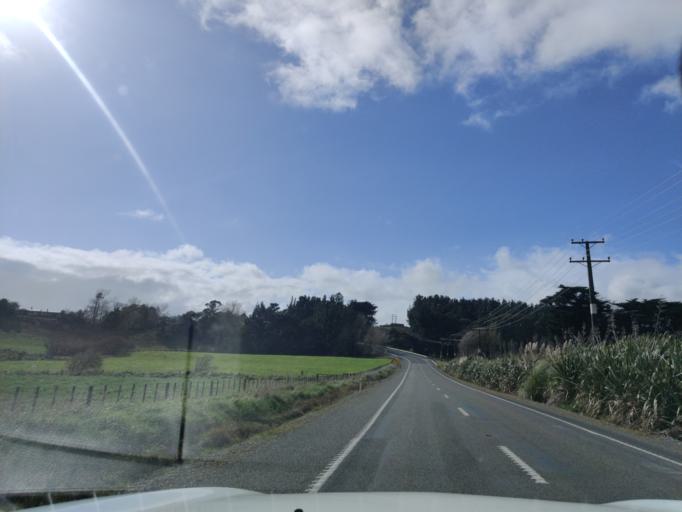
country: NZ
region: Manawatu-Wanganui
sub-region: Palmerston North City
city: Palmerston North
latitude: -40.4043
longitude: 175.6169
